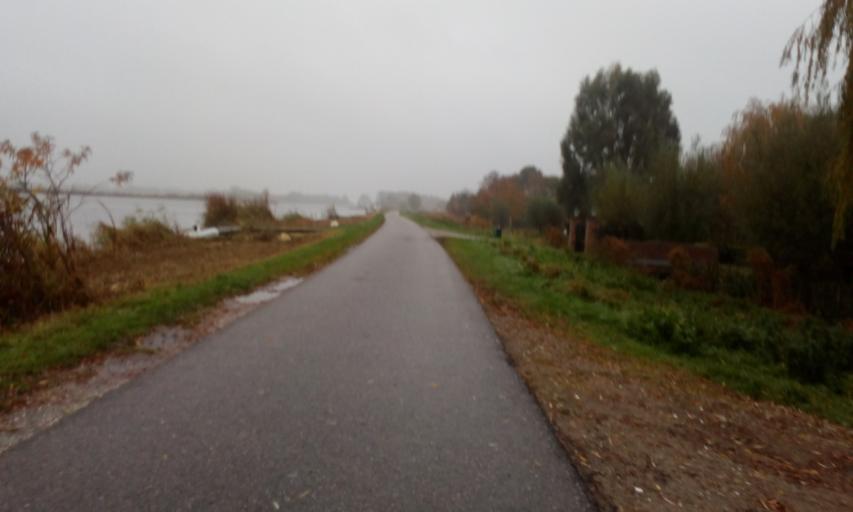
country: NL
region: South Holland
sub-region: Gemeente Lansingerland
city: Bleiswijk
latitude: 52.0227
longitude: 4.5565
